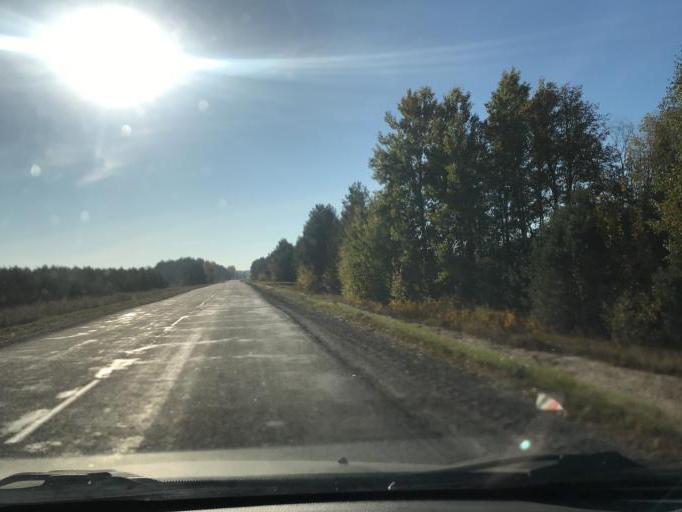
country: BY
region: Gomel
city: Brahin
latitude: 51.7541
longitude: 30.3078
